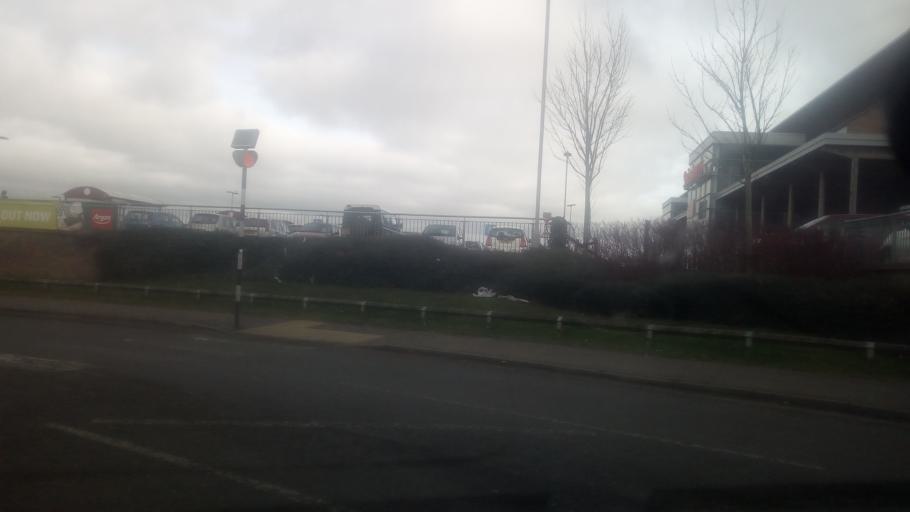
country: GB
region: Scotland
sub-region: The Scottish Borders
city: Kelso
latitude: 55.5901
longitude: -2.4280
